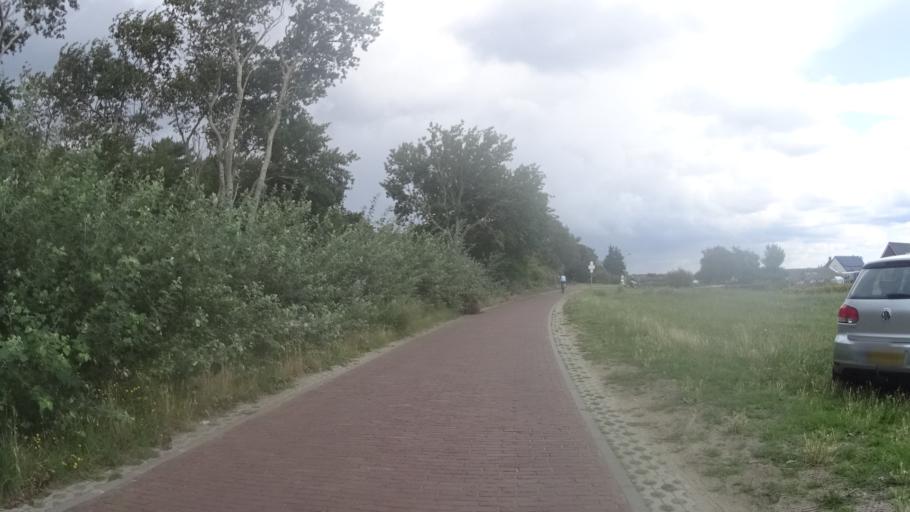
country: NL
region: North Holland
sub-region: Gemeente Bergen
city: Egmond aan Zee
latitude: 52.6118
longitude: 4.6382
